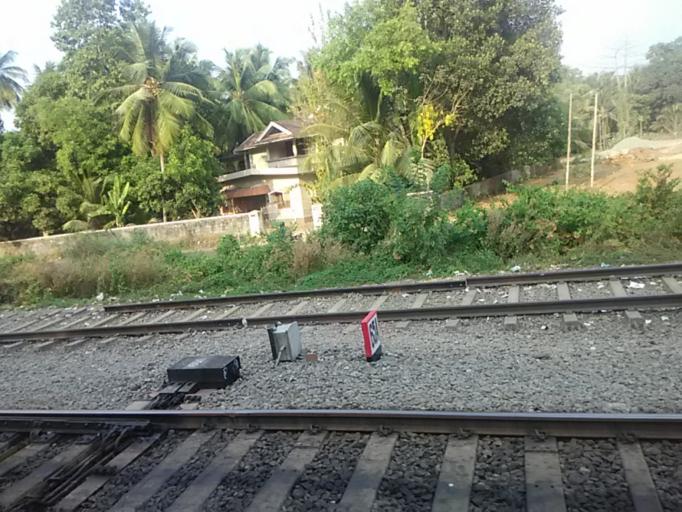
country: IN
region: Kerala
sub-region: Malappuram
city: Pariyapuram
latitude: 11.0500
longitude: 75.8589
